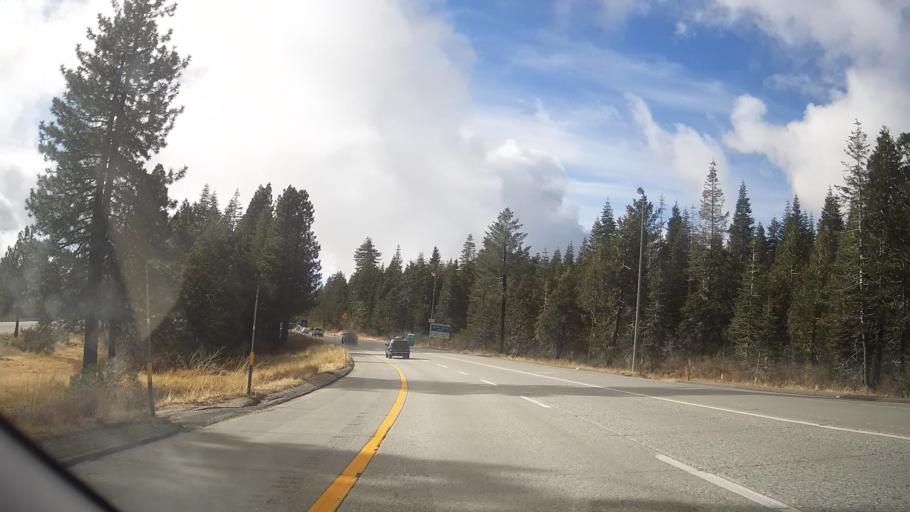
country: US
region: California
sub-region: Placer County
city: Foresthill
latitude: 39.2919
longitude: -120.6868
